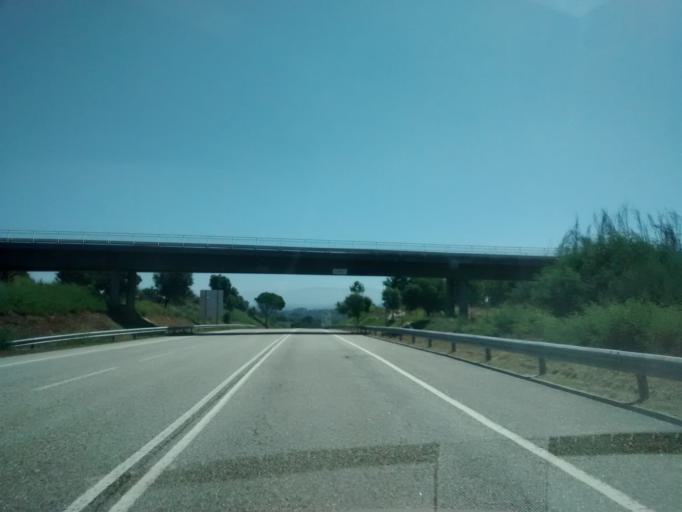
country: PT
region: Coimbra
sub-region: Tabua
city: Tabua
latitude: 40.3820
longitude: -8.0724
